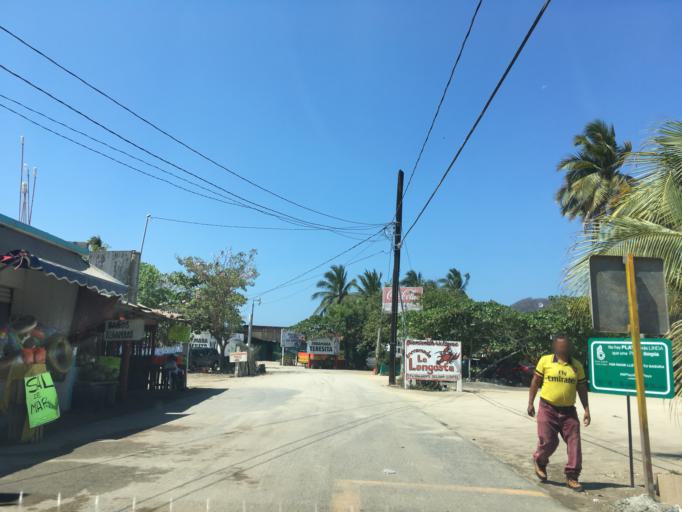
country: MX
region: Guerrero
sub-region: Zihuatanejo de Azueta
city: Los Achotes
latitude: 17.5373
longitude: -101.4421
